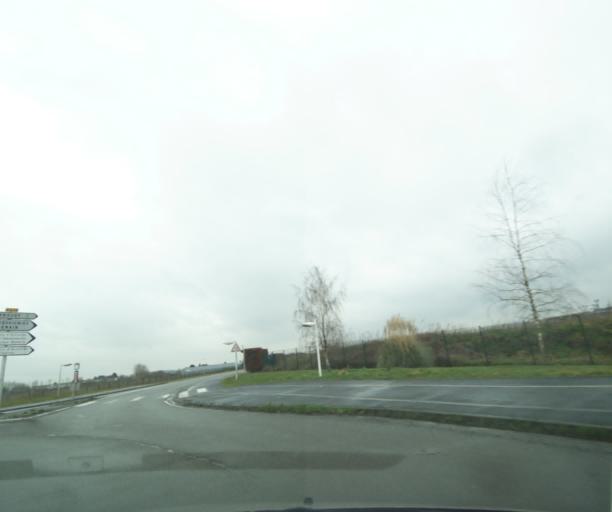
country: FR
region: Nord-Pas-de-Calais
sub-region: Departement du Nord
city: Prouvy
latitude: 50.3308
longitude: 3.4488
